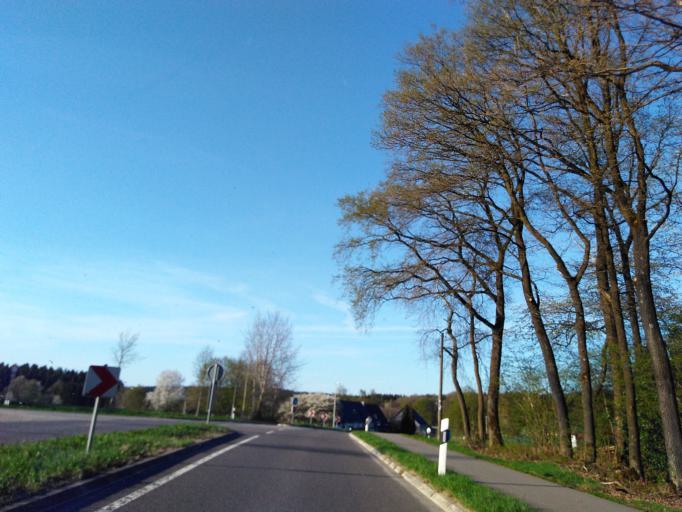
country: DE
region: North Rhine-Westphalia
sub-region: Regierungsbezirk Koln
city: Engelskirchen
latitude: 50.9538
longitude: 7.4559
